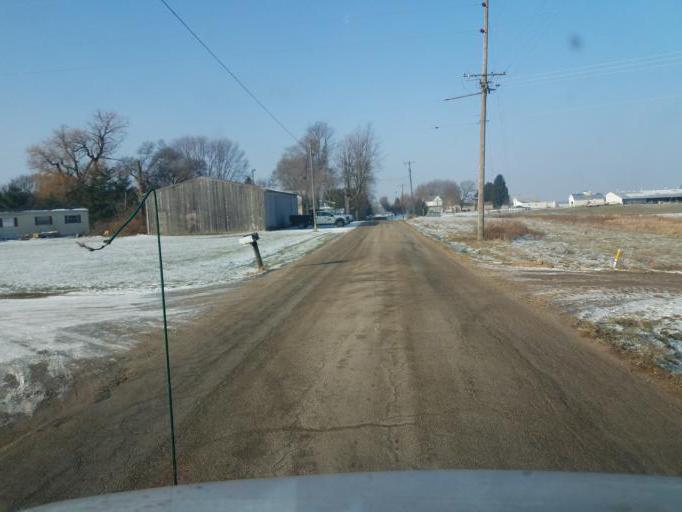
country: US
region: Ohio
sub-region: Crawford County
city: Galion
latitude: 40.6619
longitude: -82.8297
